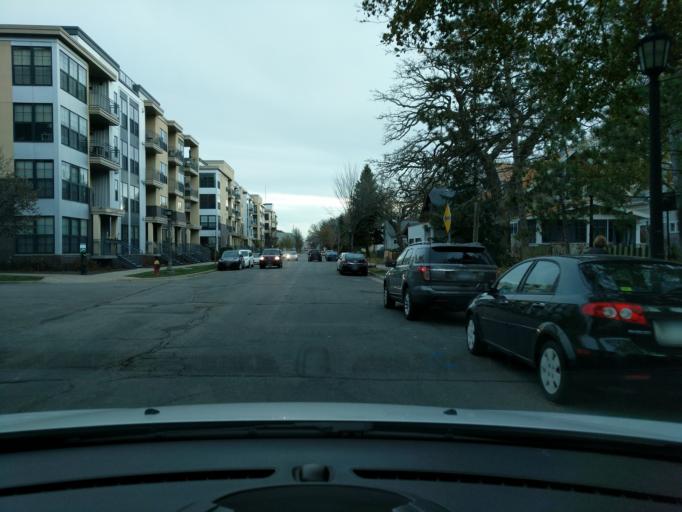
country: US
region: Minnesota
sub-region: Ramsey County
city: Lauderdale
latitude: 44.9666
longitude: -93.2078
